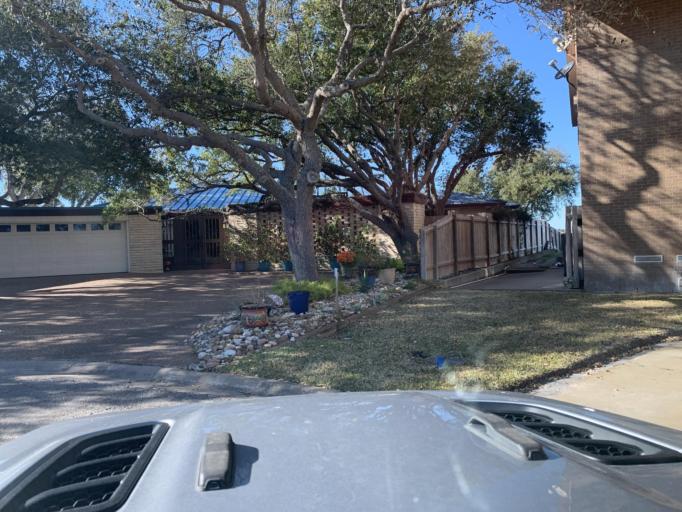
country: US
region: Texas
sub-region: Aransas County
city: Fulton
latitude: 28.0363
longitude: -97.0326
